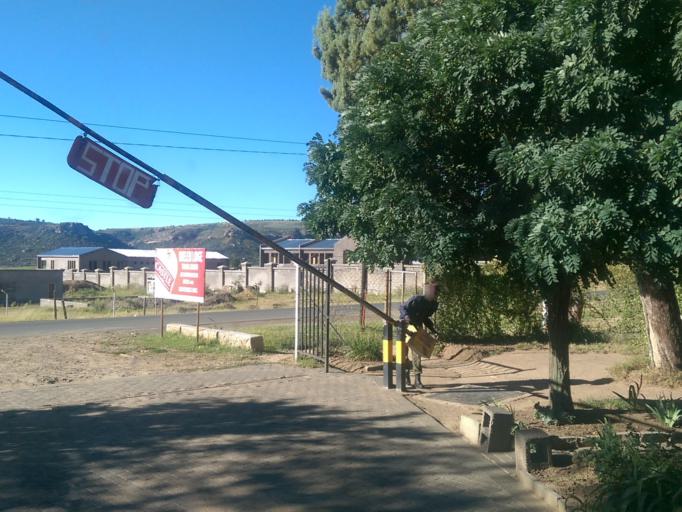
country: LS
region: Maseru
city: Maseru
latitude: -29.3500
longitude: 27.6606
